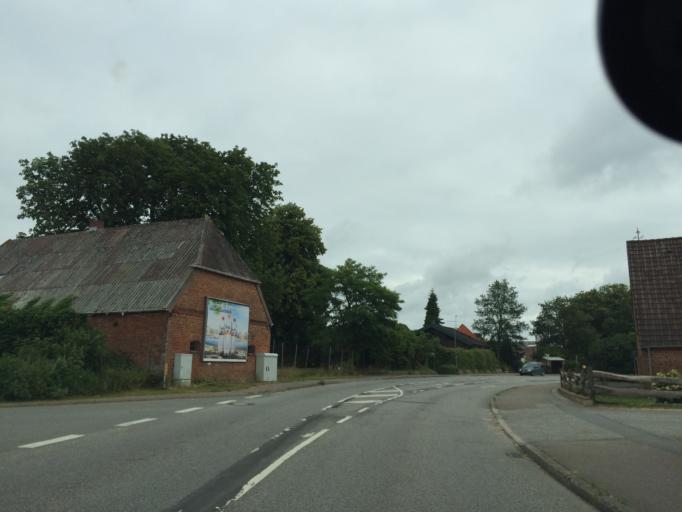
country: DE
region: Schleswig-Holstein
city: Holtsee
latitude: 54.3974
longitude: 9.8531
